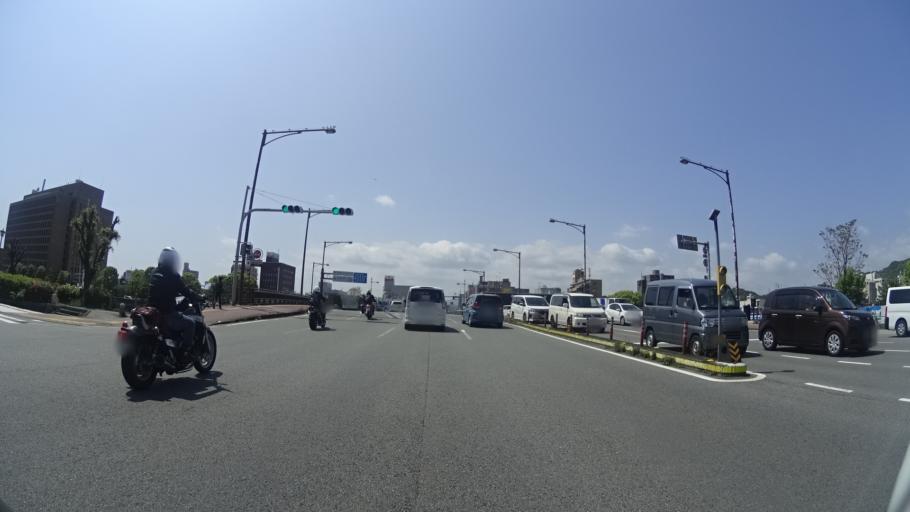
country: JP
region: Tokushima
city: Tokushima-shi
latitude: 34.0676
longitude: 134.5573
